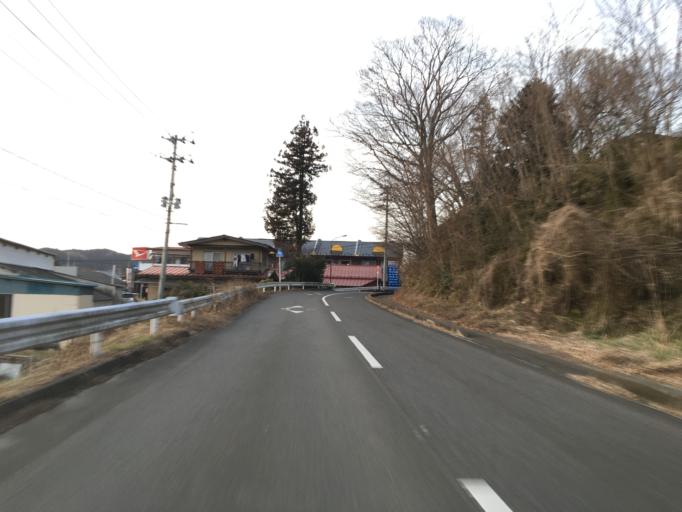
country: JP
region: Fukushima
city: Ishikawa
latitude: 37.0242
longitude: 140.3872
